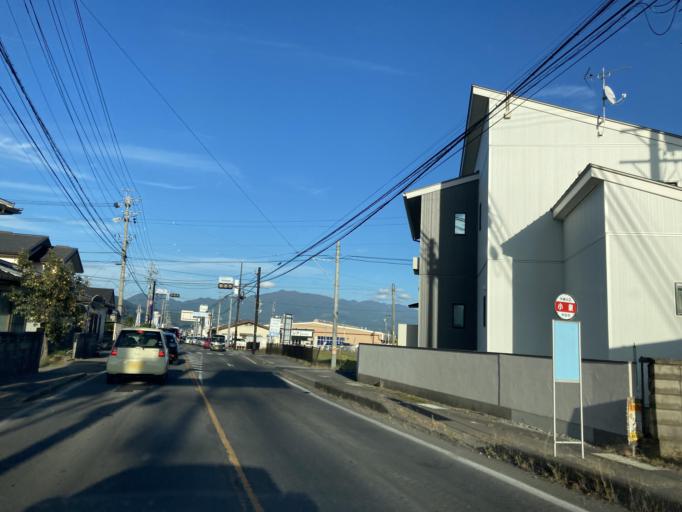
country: JP
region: Nagano
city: Ueda
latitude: 36.3835
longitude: 138.1864
